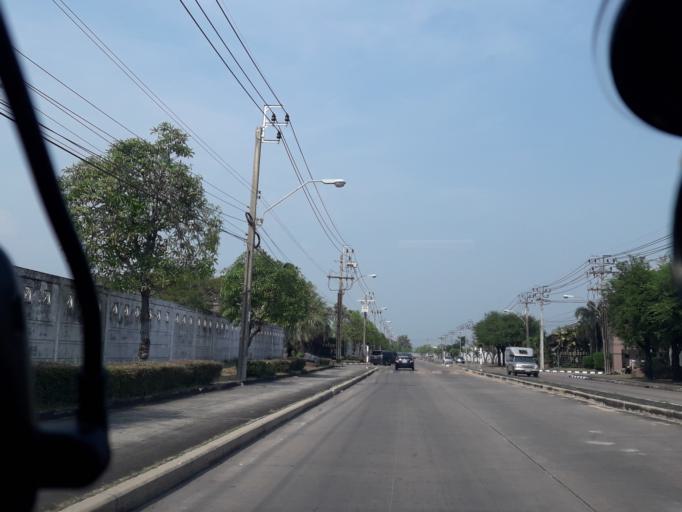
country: TH
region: Bangkok
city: Khan Na Yao
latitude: 13.8465
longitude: 100.6995
